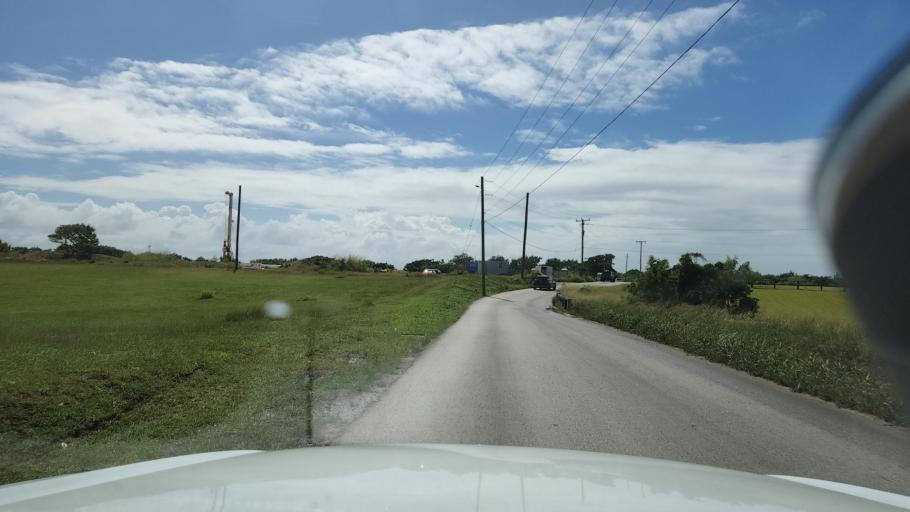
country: BB
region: Christ Church
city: Oistins
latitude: 13.0953
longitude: -59.5287
